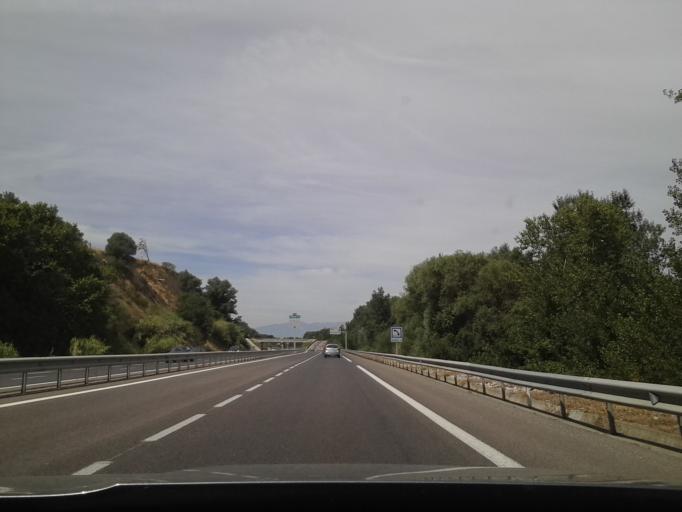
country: FR
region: Languedoc-Roussillon
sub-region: Departement des Pyrenees-Orientales
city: Baho
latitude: 42.6882
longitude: 2.8164
